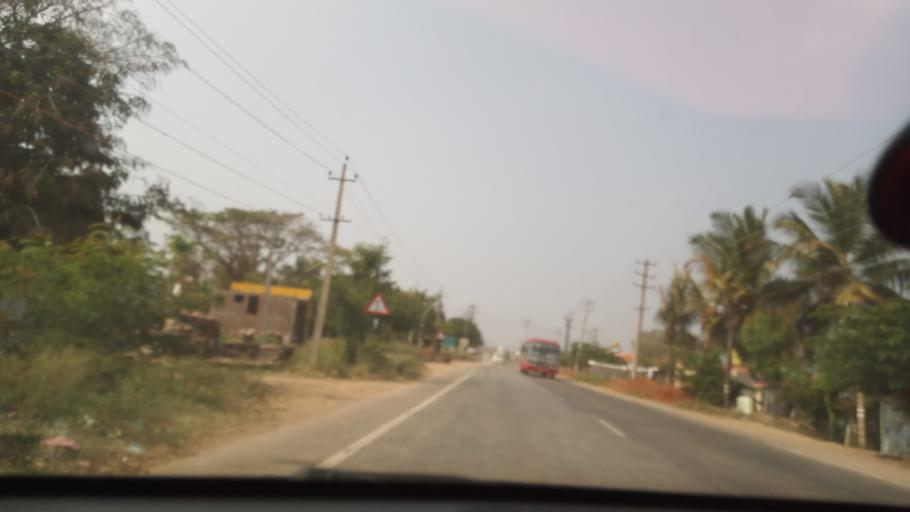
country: IN
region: Karnataka
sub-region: Chamrajnagar
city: Chamrajnagar
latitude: 11.9862
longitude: 76.8724
